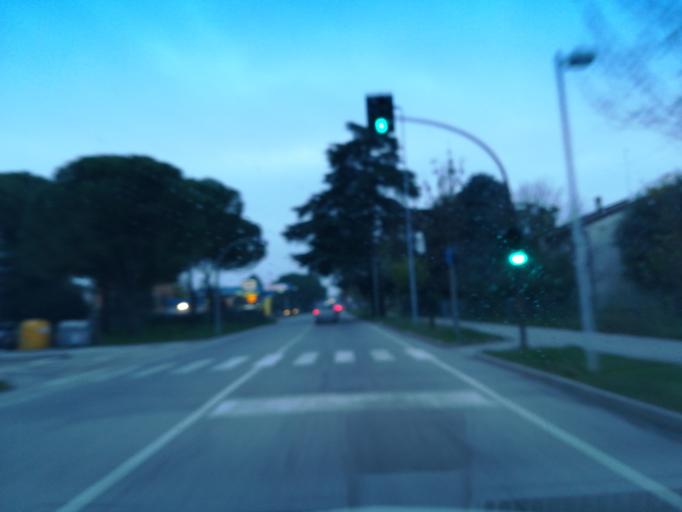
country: IT
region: Emilia-Romagna
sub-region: Provincia di Ravenna
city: Faenza
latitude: 44.2981
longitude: 11.8897
